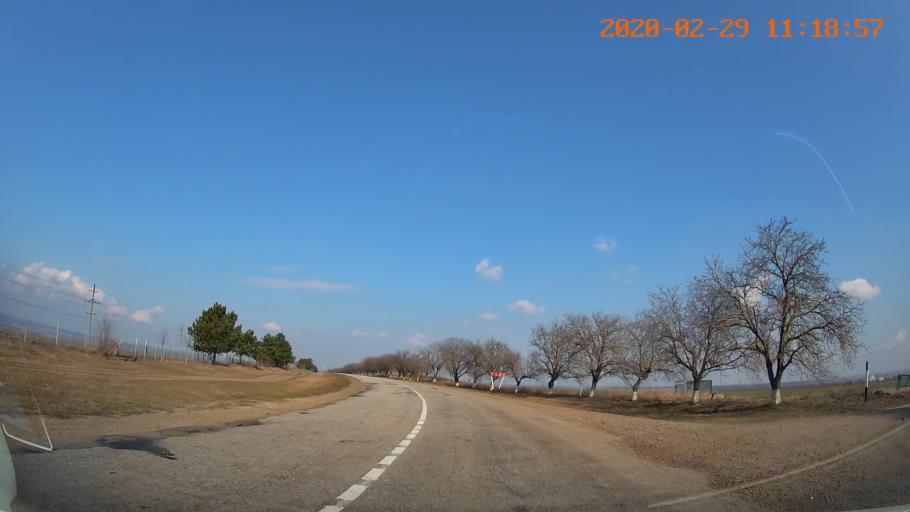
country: MD
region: Telenesti
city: Cocieri
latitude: 47.3426
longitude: 29.1761
